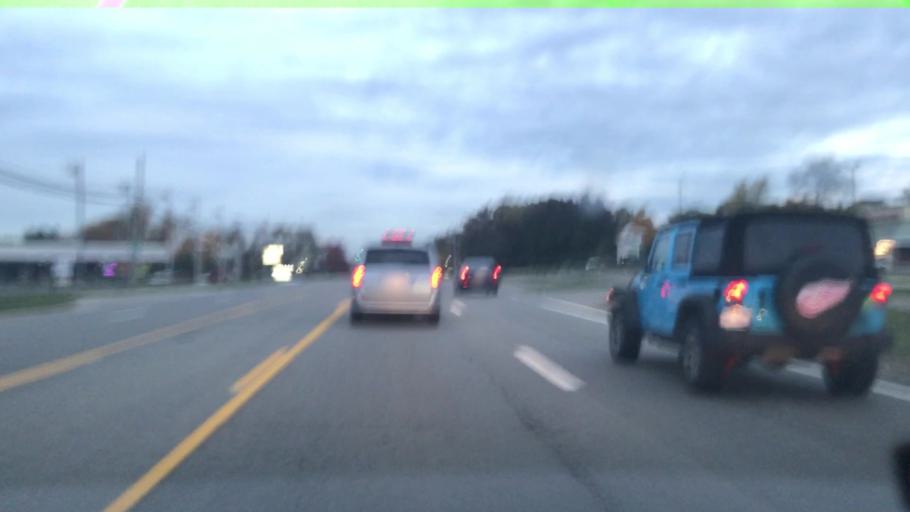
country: US
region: Michigan
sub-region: Oakland County
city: Bloomfield Hills
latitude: 42.6244
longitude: -83.2489
